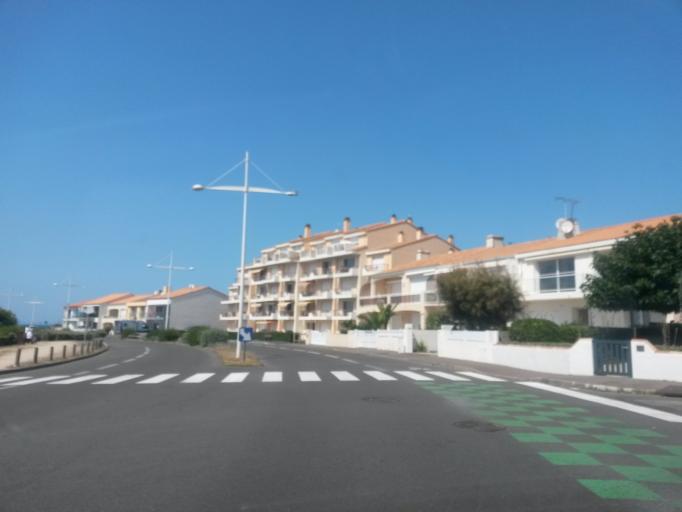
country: FR
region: Pays de la Loire
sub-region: Departement de la Vendee
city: Les Sables-d'Olonne
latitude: 46.4922
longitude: -1.8069
